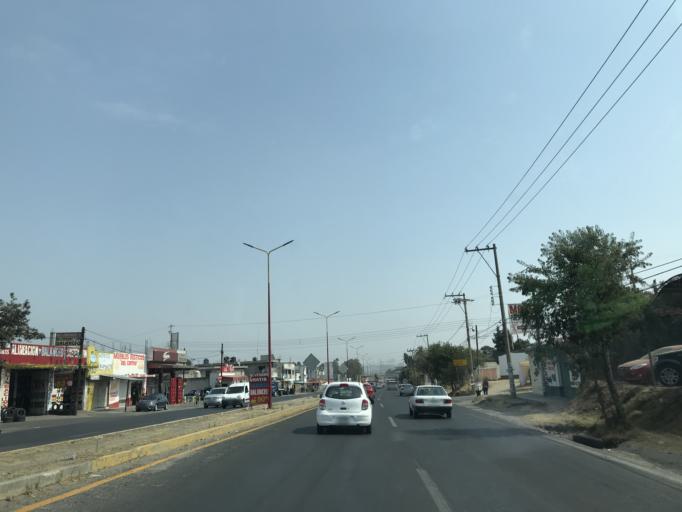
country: MX
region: Tlaxcala
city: La Magdalena Tlaltelulco
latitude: 19.2881
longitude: -98.1951
